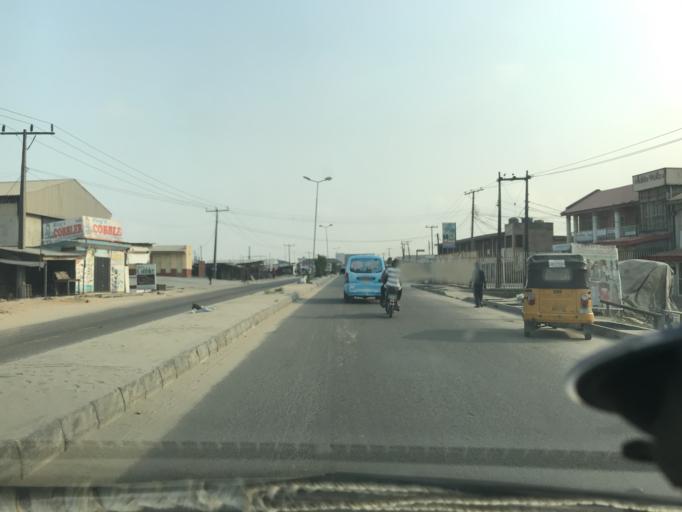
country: NG
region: Lagos
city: Ikoyi
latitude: 6.4832
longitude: 3.5735
